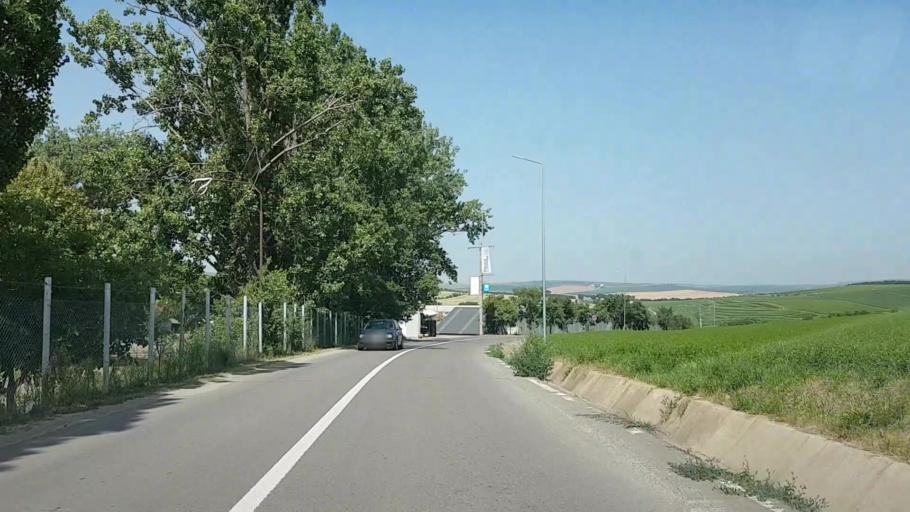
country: RO
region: Cluj
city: Turda
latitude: 46.5844
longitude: 23.7990
